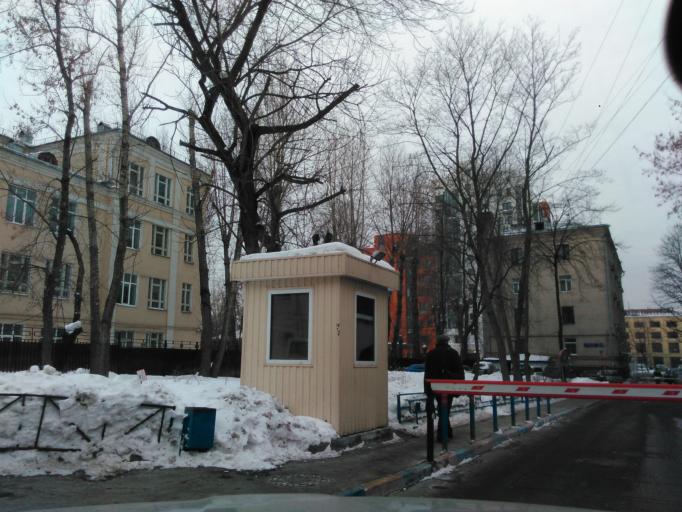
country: RU
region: Moskovskaya
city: Dorogomilovo
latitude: 55.7678
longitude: 37.5687
